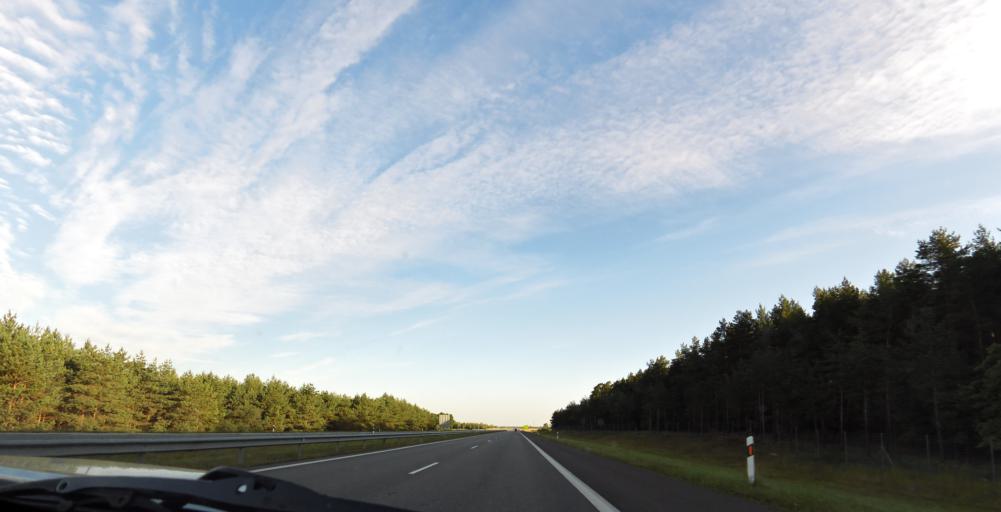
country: LT
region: Vilnius County
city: Ukmerge
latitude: 55.2774
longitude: 24.8075
